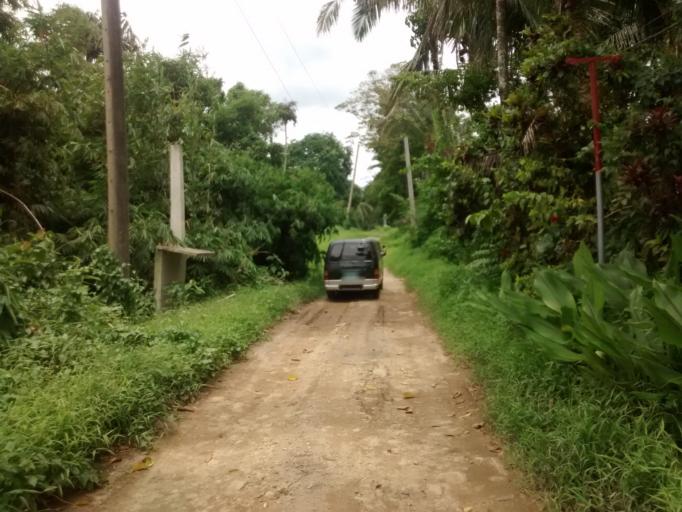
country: PH
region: Calabarzon
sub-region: Province of Quezon
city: Lucban
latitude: 14.1584
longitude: 121.5498
